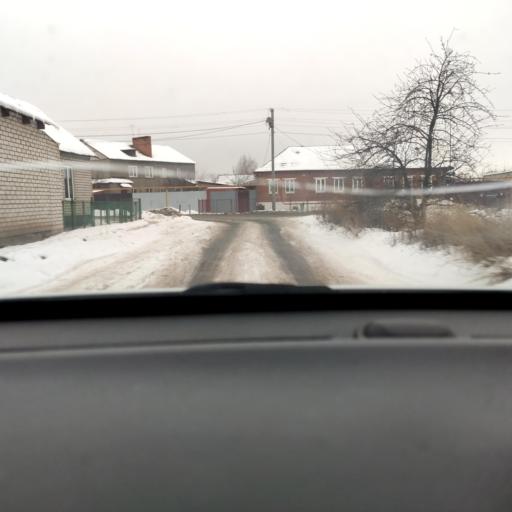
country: RU
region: Voronezj
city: Somovo
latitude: 51.7477
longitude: 39.3384
